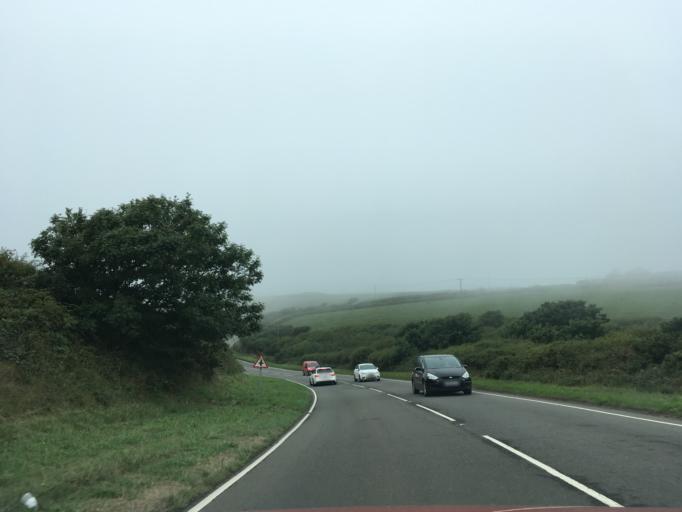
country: GB
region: Wales
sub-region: Pembrokeshire
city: Llanrhian
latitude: 51.8762
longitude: -5.1690
